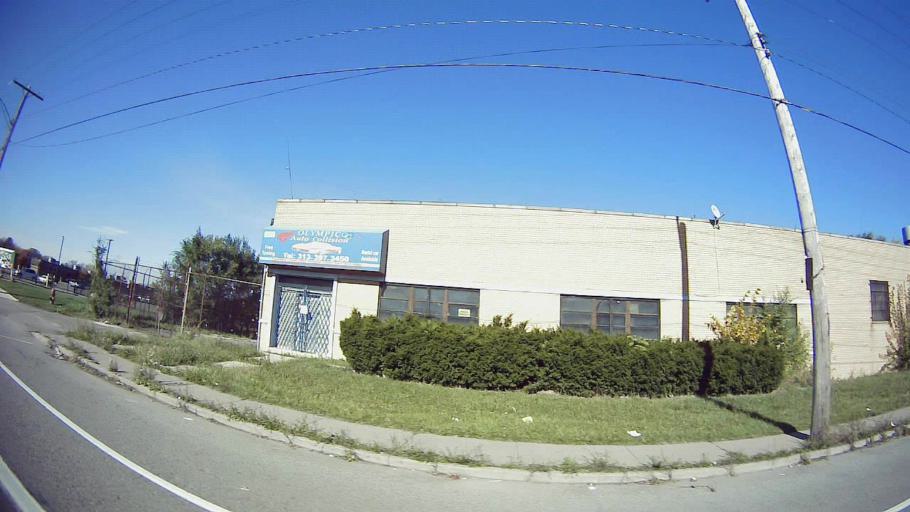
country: US
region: Michigan
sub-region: Wayne County
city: Dearborn
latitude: 42.3665
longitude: -83.1546
